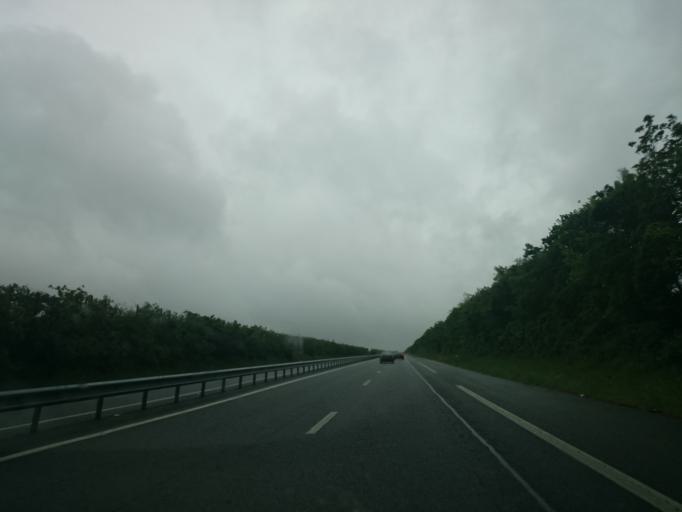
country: FR
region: Brittany
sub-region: Departement d'Ille-et-Vilaine
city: Plelan-le-Grand
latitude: 47.9871
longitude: -2.0979
